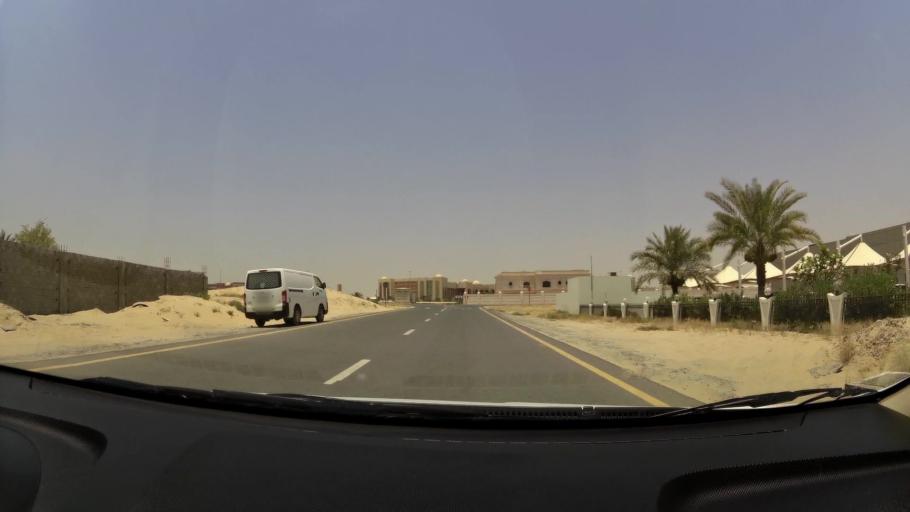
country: AE
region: Ajman
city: Ajman
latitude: 25.4084
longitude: 55.5056
